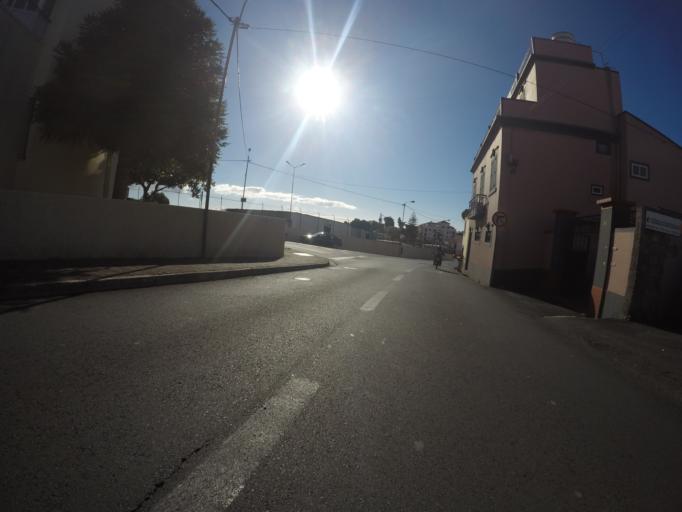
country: PT
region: Madeira
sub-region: Funchal
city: Nossa Senhora do Monte
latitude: 32.6553
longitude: -16.9251
